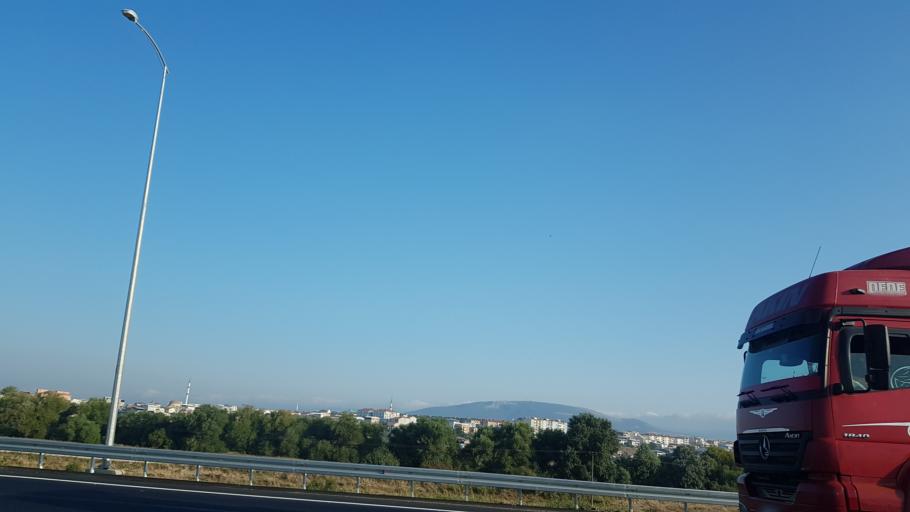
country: TR
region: Bursa
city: Karacabey
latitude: 40.1978
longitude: 28.3683
